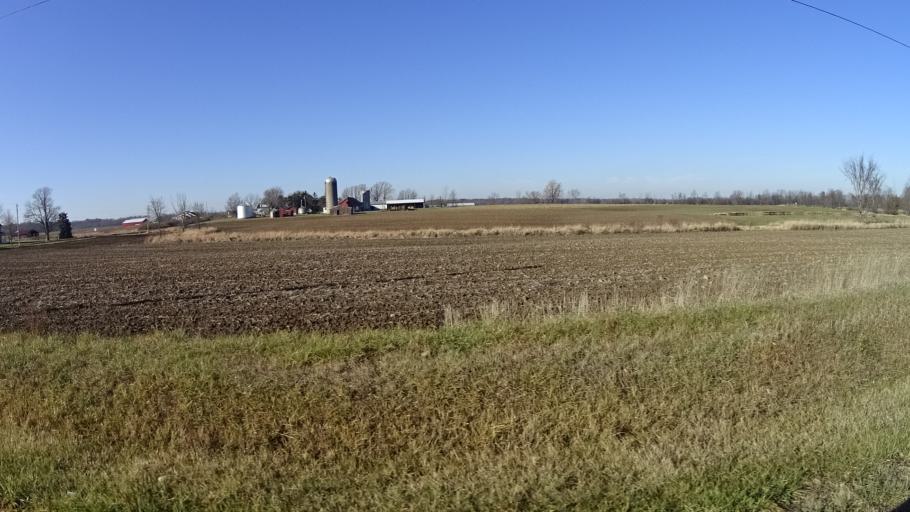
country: US
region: Ohio
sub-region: Lorain County
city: Wellington
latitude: 41.0855
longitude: -82.1811
